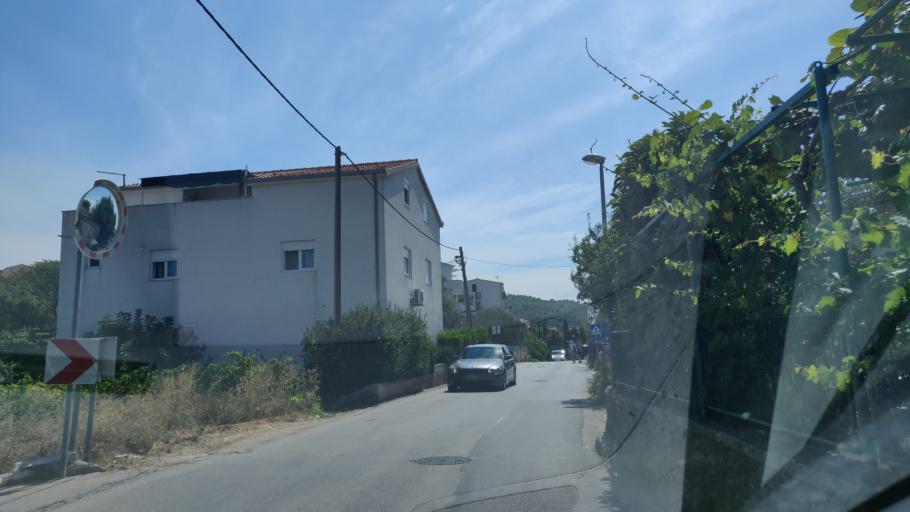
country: HR
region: Splitsko-Dalmatinska
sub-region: Grad Trogir
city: Trogir
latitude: 43.5120
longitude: 16.2508
